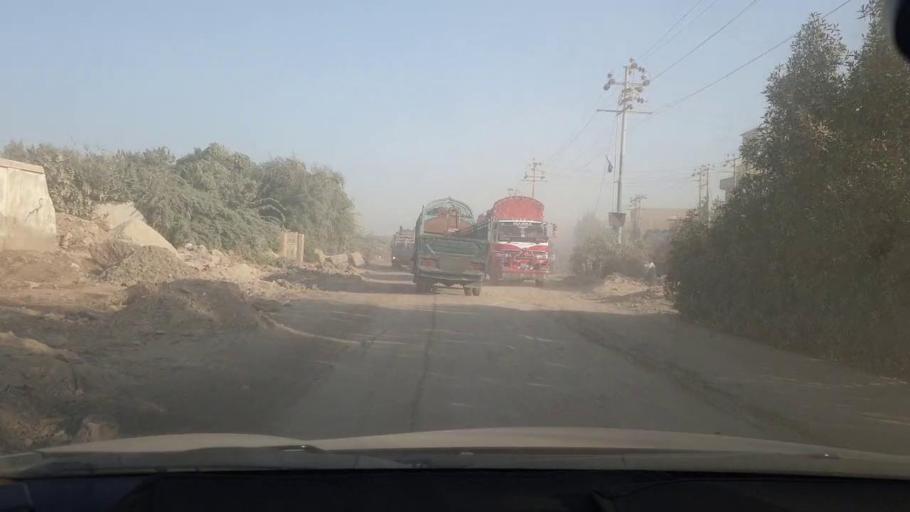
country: PK
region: Sindh
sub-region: Karachi District
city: Karachi
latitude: 24.9722
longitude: 67.0397
